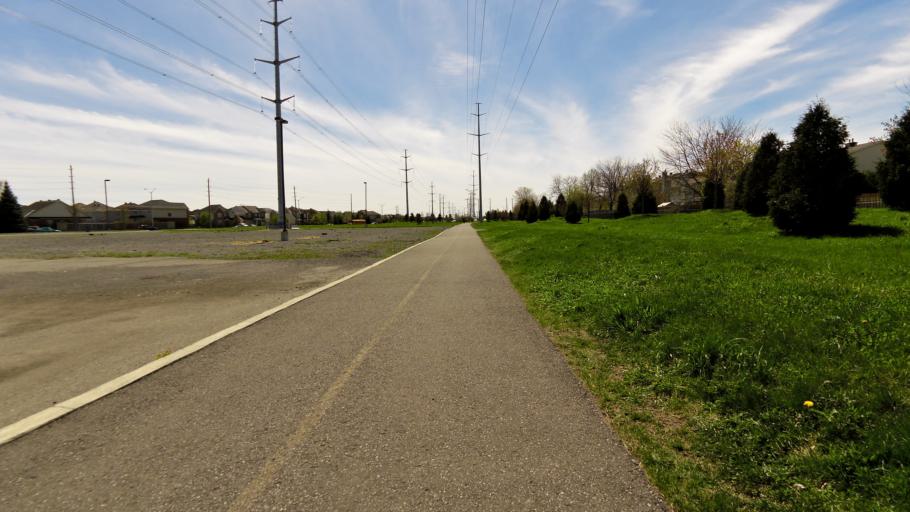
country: CA
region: Ontario
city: Clarence-Rockland
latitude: 45.4666
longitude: -75.4732
